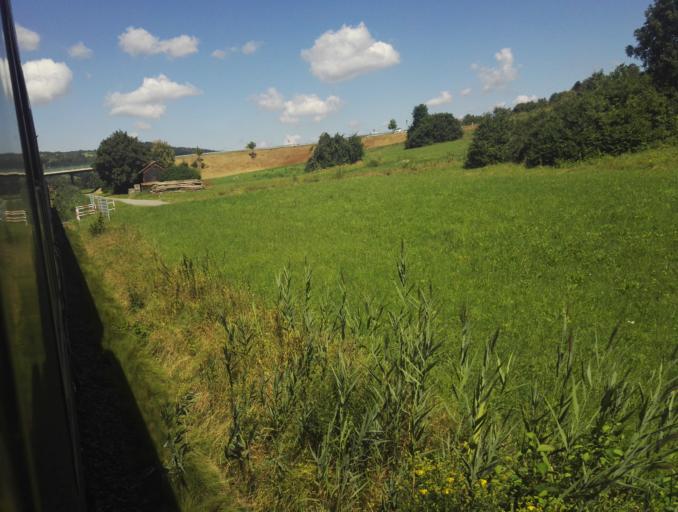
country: DE
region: Baden-Wuerttemberg
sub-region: Regierungsbezirk Stuttgart
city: Schorndorf
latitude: 48.8356
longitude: 9.5452
